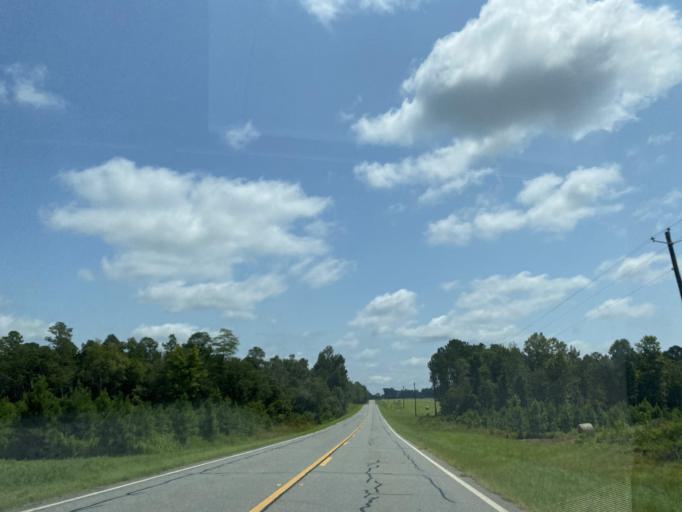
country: US
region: Georgia
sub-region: Wilcox County
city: Abbeville
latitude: 32.0050
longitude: -83.1326
